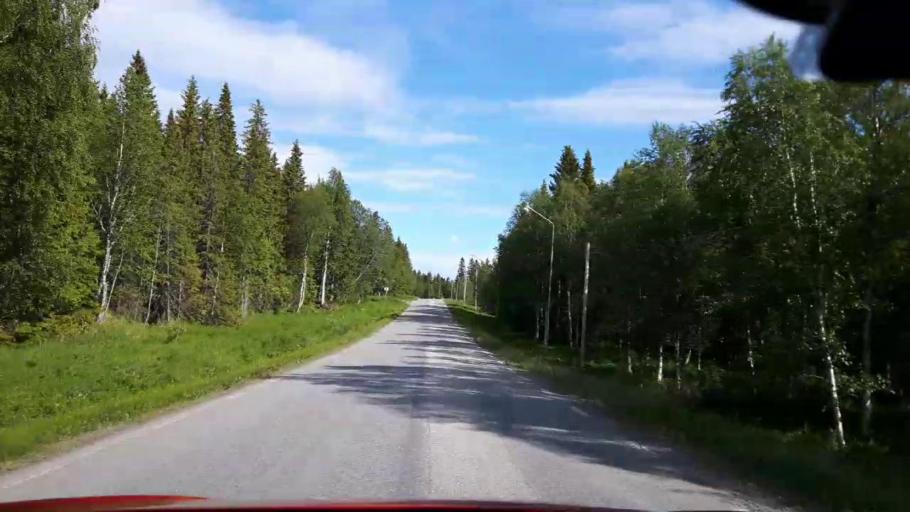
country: SE
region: Jaemtland
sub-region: Krokoms Kommun
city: Valla
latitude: 63.7707
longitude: 14.0525
